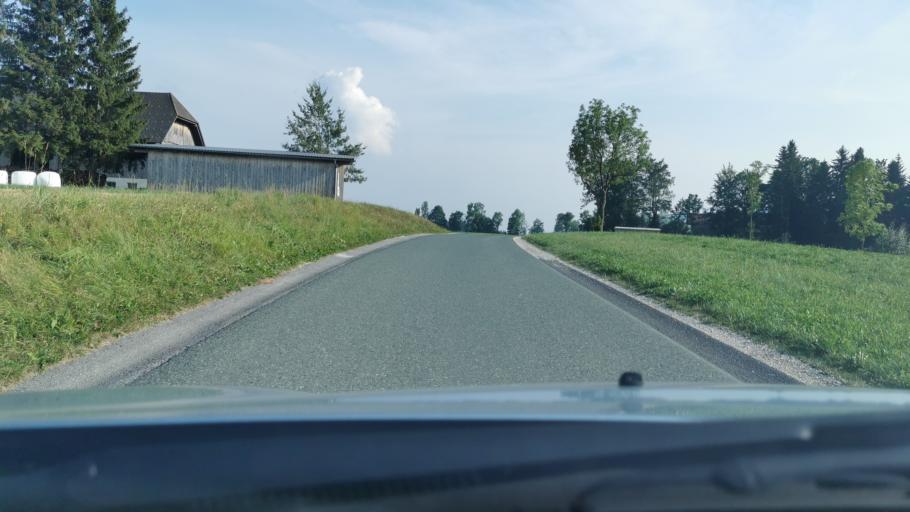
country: AT
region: Styria
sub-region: Politischer Bezirk Weiz
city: Birkfeld
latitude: 47.3700
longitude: 15.6668
